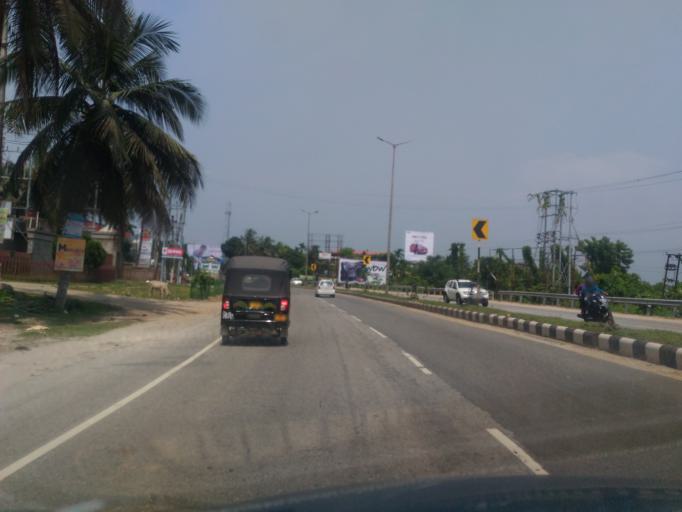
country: IN
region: Assam
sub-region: Kamrup
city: Soalkuchi
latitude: 26.1373
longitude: 91.6325
